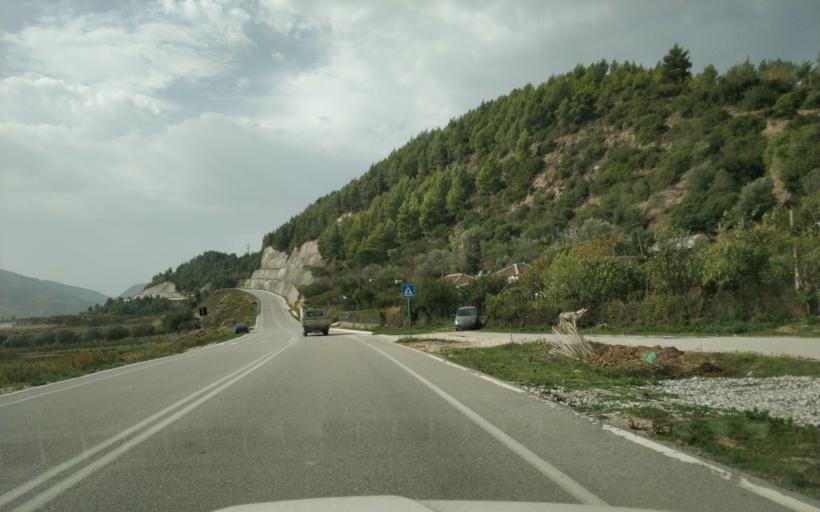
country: AL
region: Gjirokaster
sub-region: Rrethi i Tepelenes
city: Krahes
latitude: 40.3820
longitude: 19.8987
